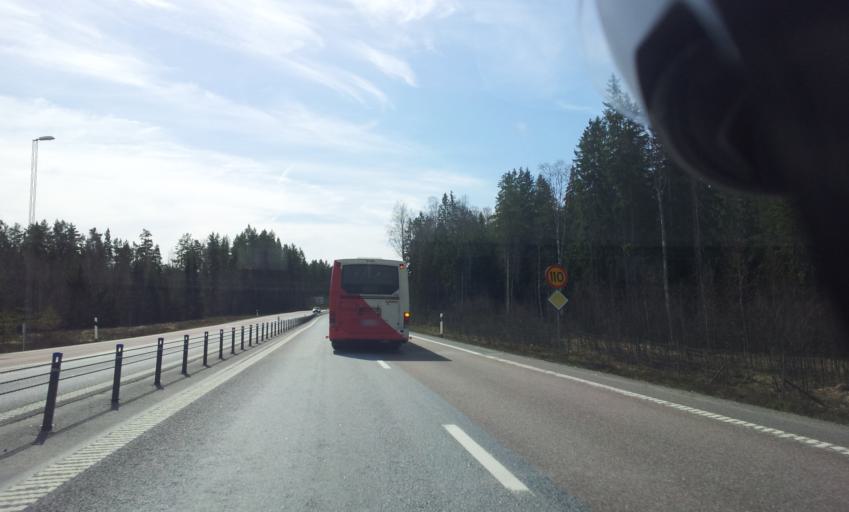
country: SE
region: Gaevleborg
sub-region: Gavle Kommun
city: Norrsundet
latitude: 61.0693
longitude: 16.9642
